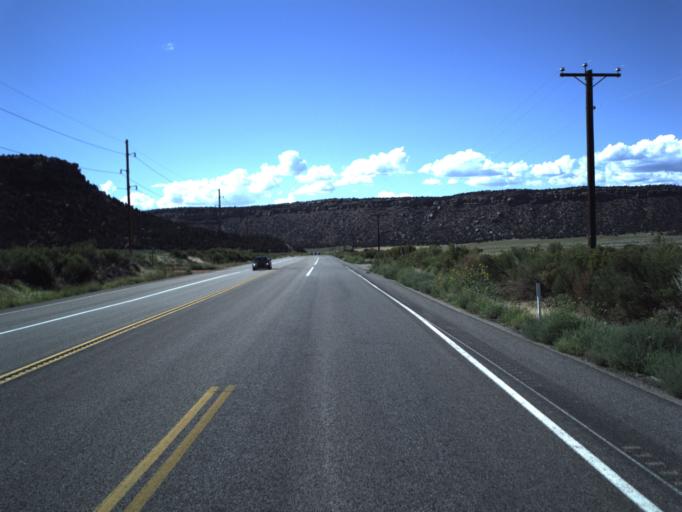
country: US
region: Utah
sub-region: Washington County
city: LaVerkin
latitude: 37.1096
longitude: -113.1448
